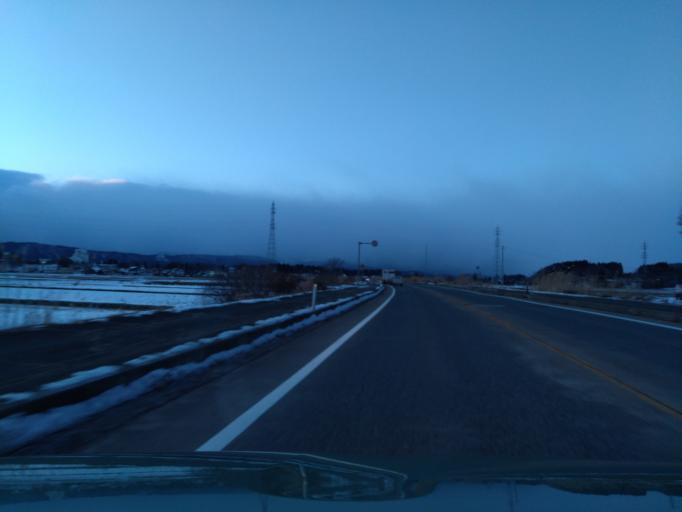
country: JP
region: Iwate
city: Shizukuishi
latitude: 39.7003
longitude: 140.9758
